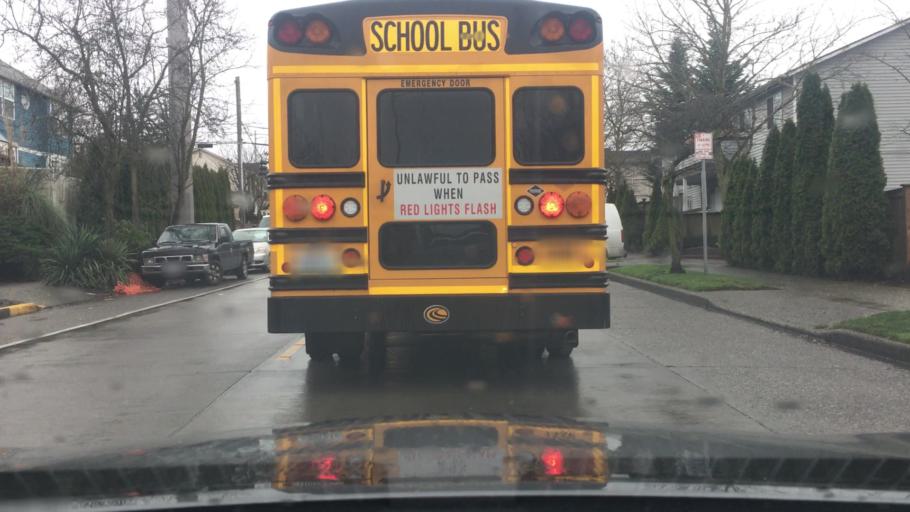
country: US
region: Washington
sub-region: King County
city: White Center
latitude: 47.5252
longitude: -122.3605
